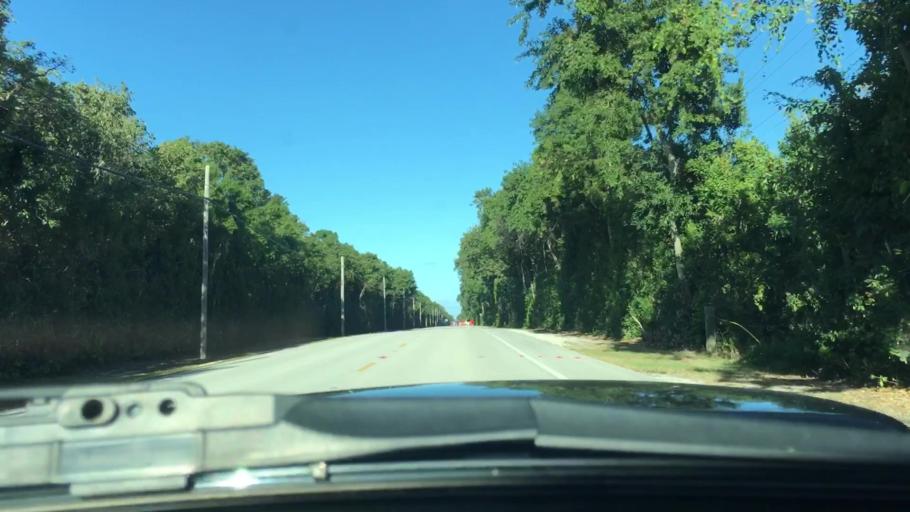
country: US
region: Florida
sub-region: Monroe County
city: North Key Largo
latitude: 25.1824
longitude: -80.3642
